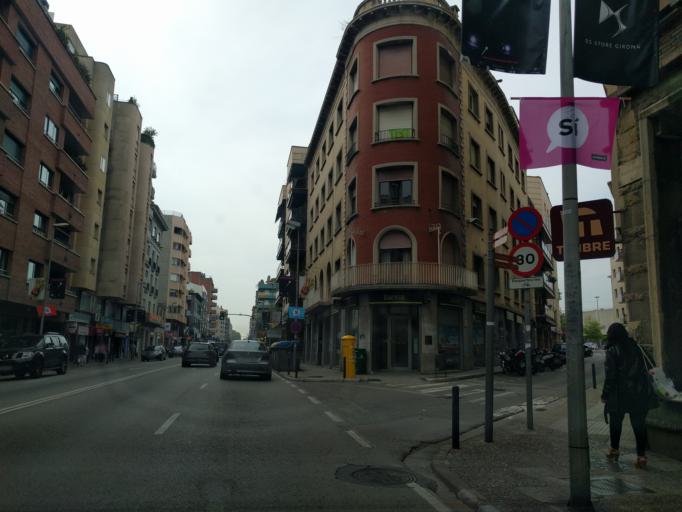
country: ES
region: Catalonia
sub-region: Provincia de Girona
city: Girona
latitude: 41.9801
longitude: 2.8184
